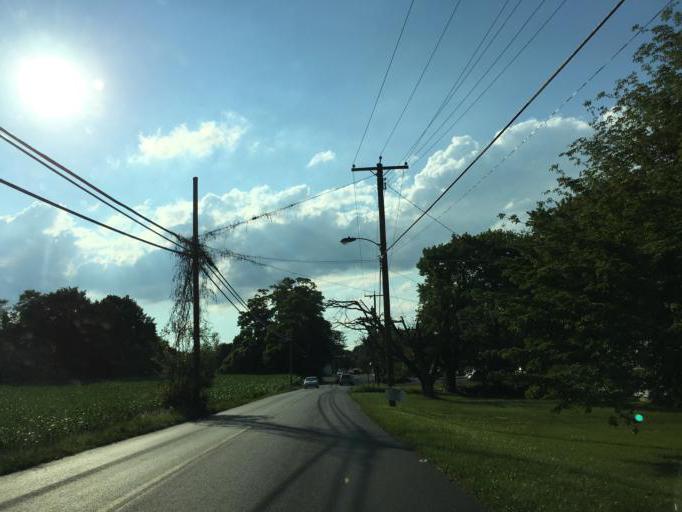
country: US
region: Maryland
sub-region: Baltimore County
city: Kingsville
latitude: 39.4673
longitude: -76.4402
